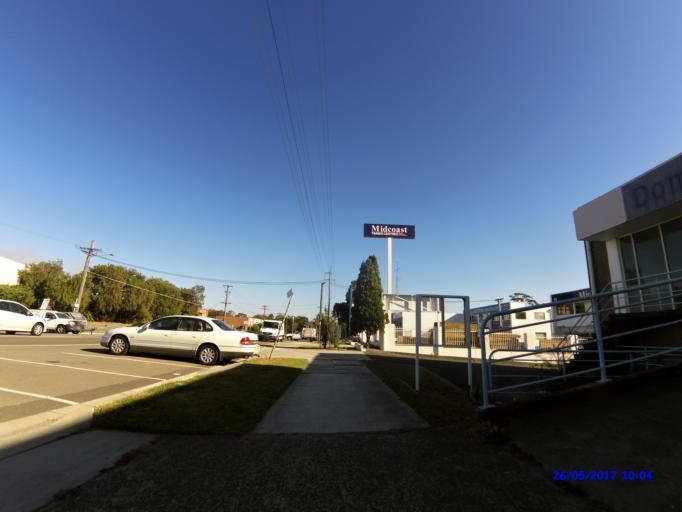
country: AU
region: New South Wales
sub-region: Sutherland Shire
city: Kirrawee
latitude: -34.0285
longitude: 151.0743
